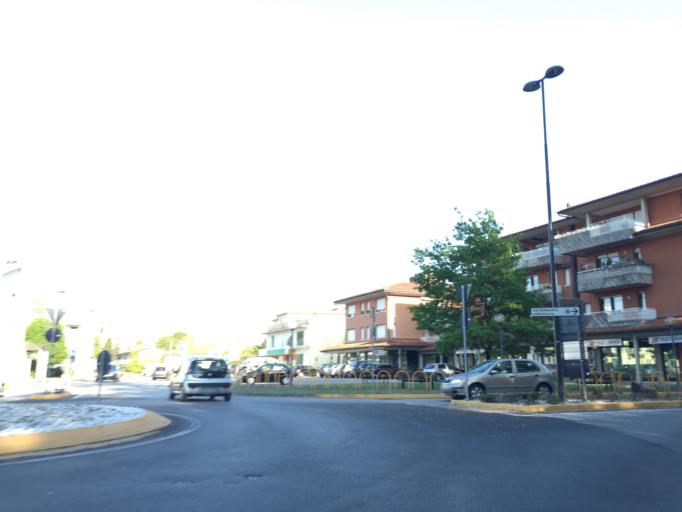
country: IT
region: Friuli Venezia Giulia
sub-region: Provincia di Pordenone
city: Porcia
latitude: 45.9573
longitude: 12.6183
